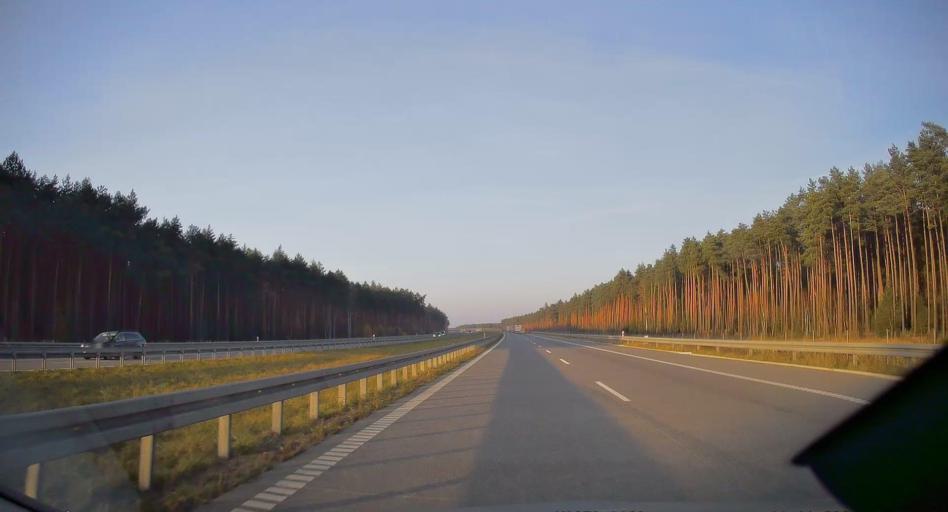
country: PL
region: Silesian Voivodeship
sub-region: Powiat tarnogorski
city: Ozarowice
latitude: 50.5170
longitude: 19.0652
